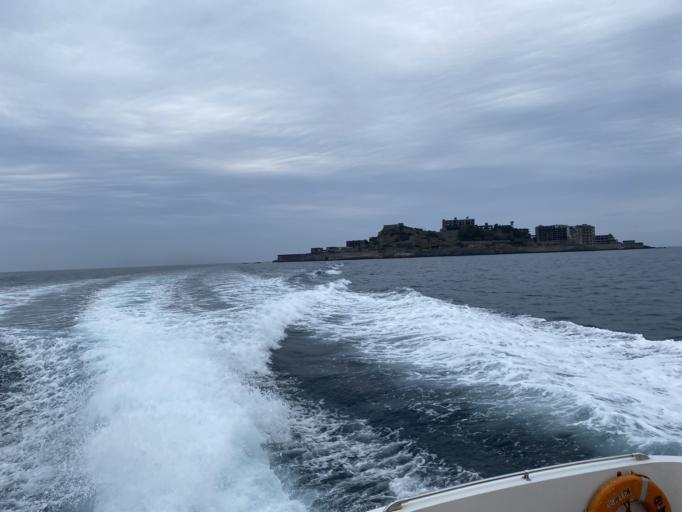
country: JP
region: Nagasaki
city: Nagasaki-shi
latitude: 32.6237
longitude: 129.7444
